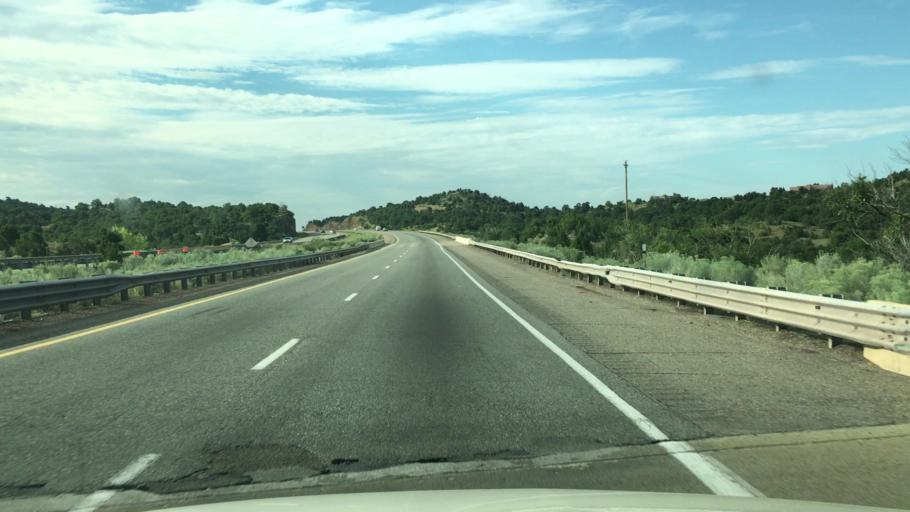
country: US
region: New Mexico
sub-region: Santa Fe County
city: Santa Fe
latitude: 35.6211
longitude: -105.9198
